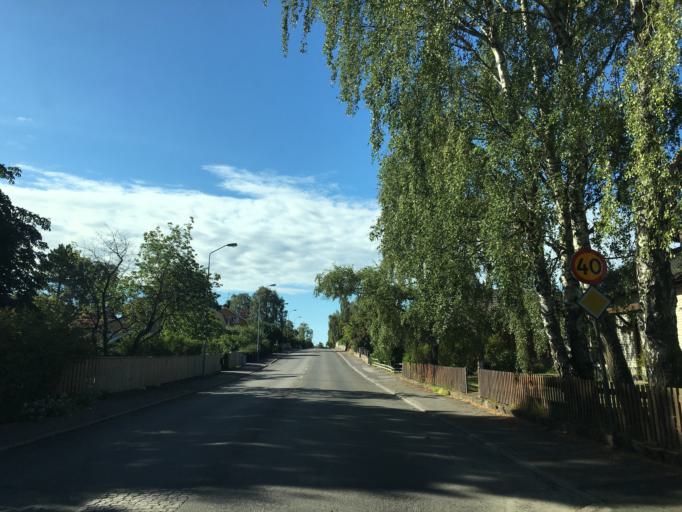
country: SE
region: Kalmar
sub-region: Kalmar Kommun
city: Kalmar
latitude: 56.6925
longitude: 16.3560
